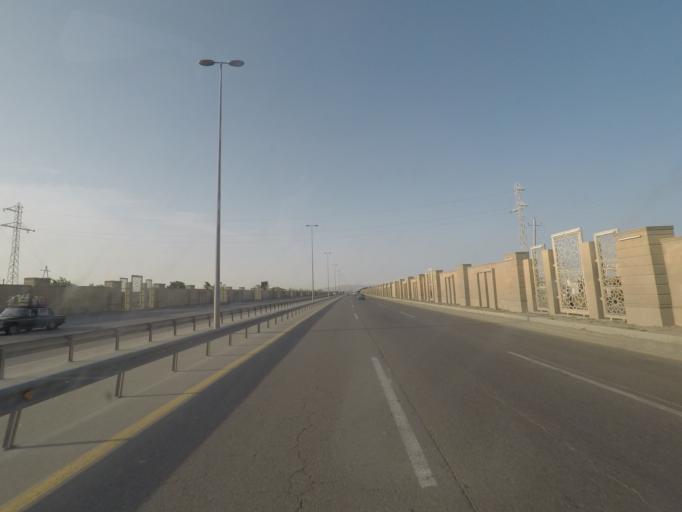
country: AZ
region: Baki
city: Qobustan
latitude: 40.0918
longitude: 49.4184
